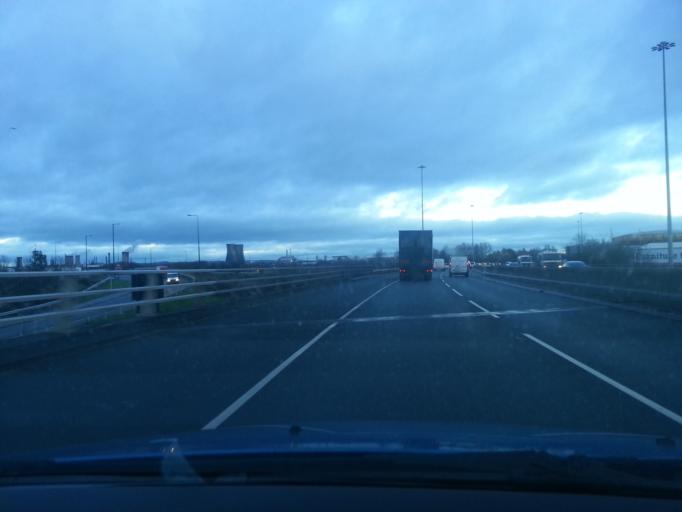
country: GB
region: England
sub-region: Middlesbrough
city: Middlesbrough
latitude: 54.5716
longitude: -1.2565
